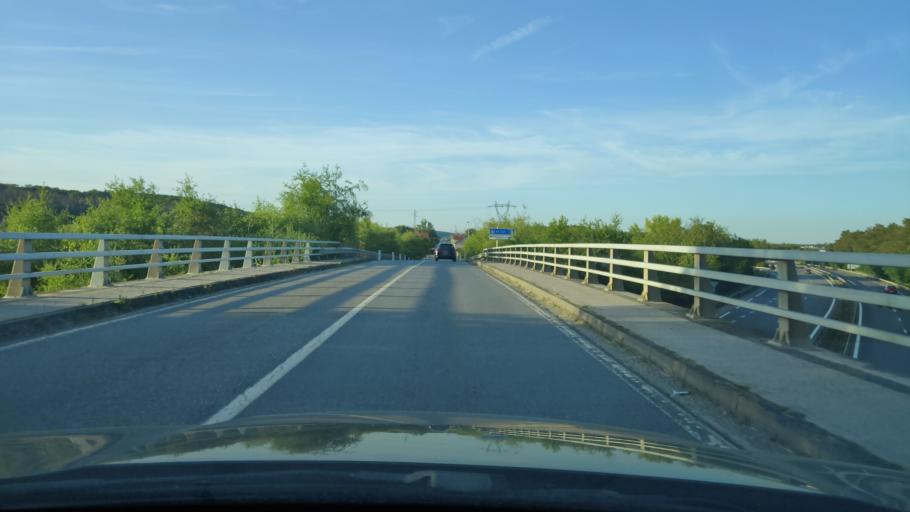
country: FR
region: Lorraine
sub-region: Departement de la Moselle
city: Maizieres-les-Metz
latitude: 49.2068
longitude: 6.1487
